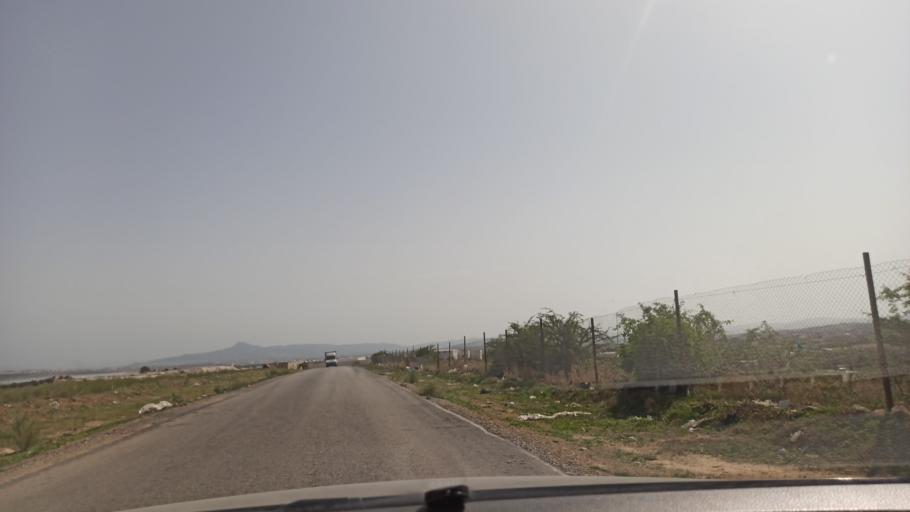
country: TN
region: Manouba
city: Manouba
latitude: 36.7343
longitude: 10.0915
